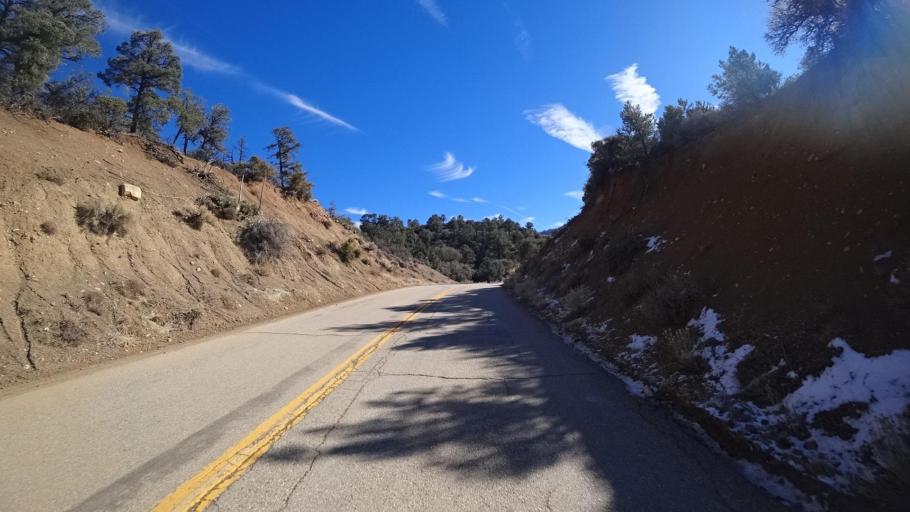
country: US
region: California
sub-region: Kern County
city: Pine Mountain Club
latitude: 34.8654
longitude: -119.2308
